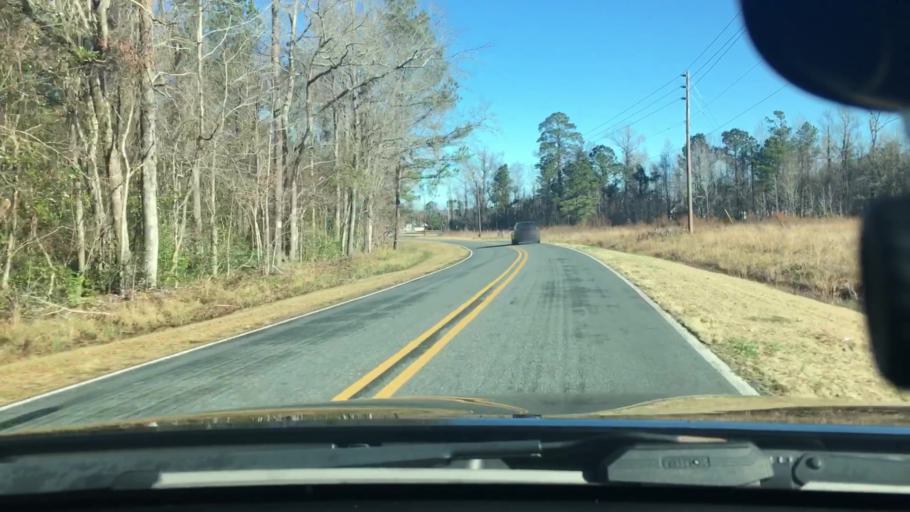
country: US
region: North Carolina
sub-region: Craven County
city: New Bern
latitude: 35.1924
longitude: -77.0552
